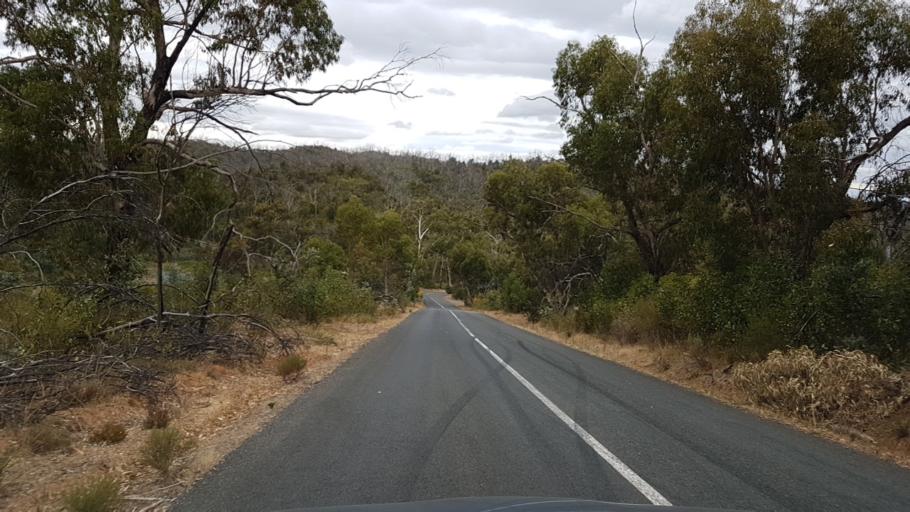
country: AU
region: South Australia
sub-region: Adelaide Hills
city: Gumeracha
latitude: -34.7699
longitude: 138.8224
